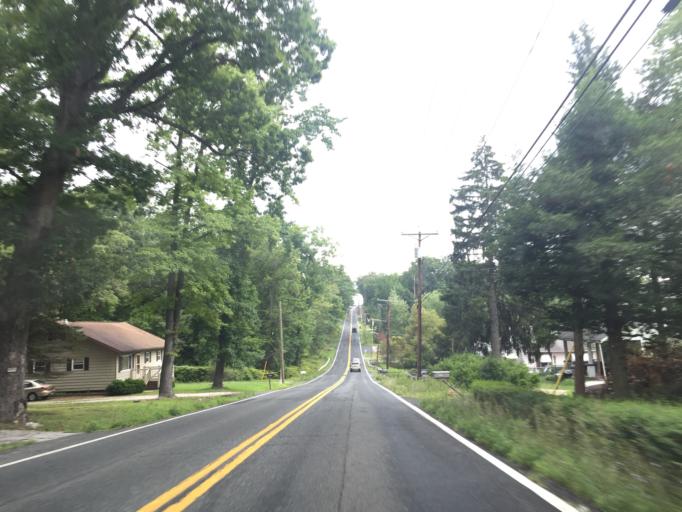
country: US
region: Maryland
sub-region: Baltimore County
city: White Marsh
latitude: 39.3947
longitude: -76.4234
